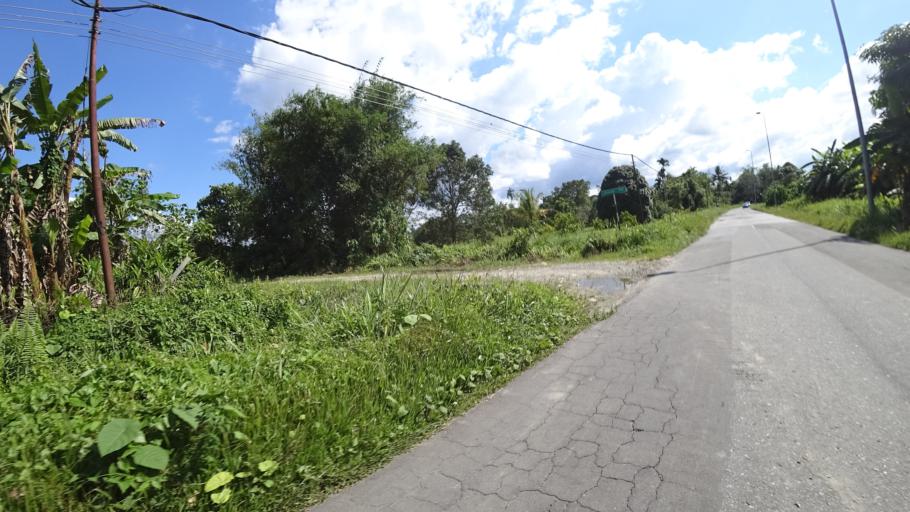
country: BN
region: Tutong
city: Tutong
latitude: 4.7647
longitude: 114.7957
